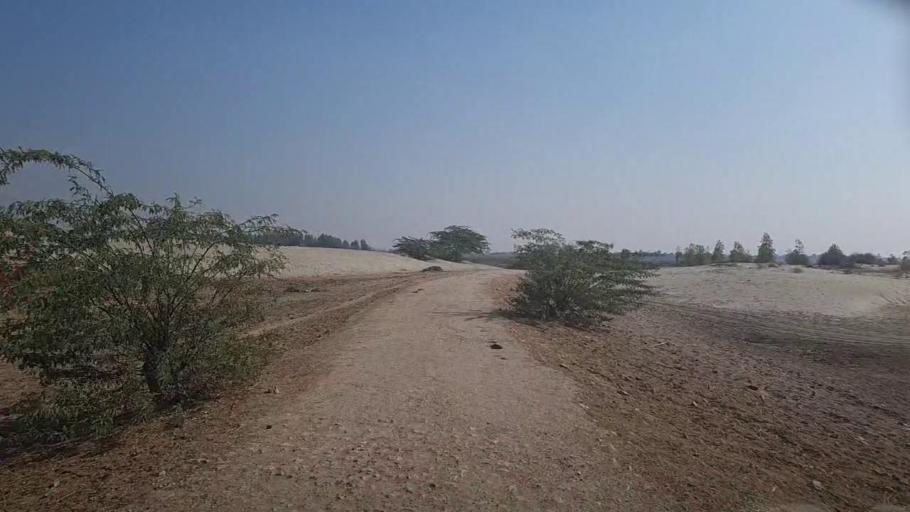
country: PK
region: Sindh
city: Kot Diji
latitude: 27.4315
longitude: 68.7256
